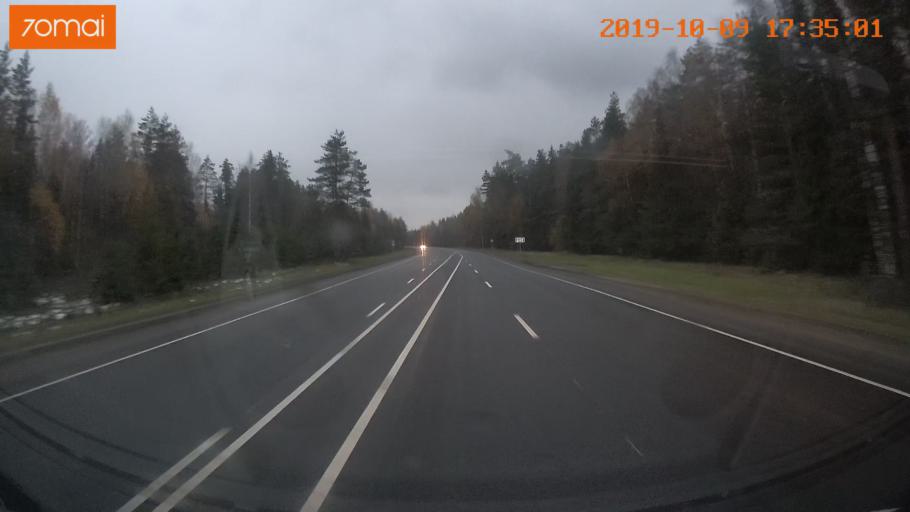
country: RU
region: Ivanovo
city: Bogorodskoye
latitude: 57.1000
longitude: 41.0060
